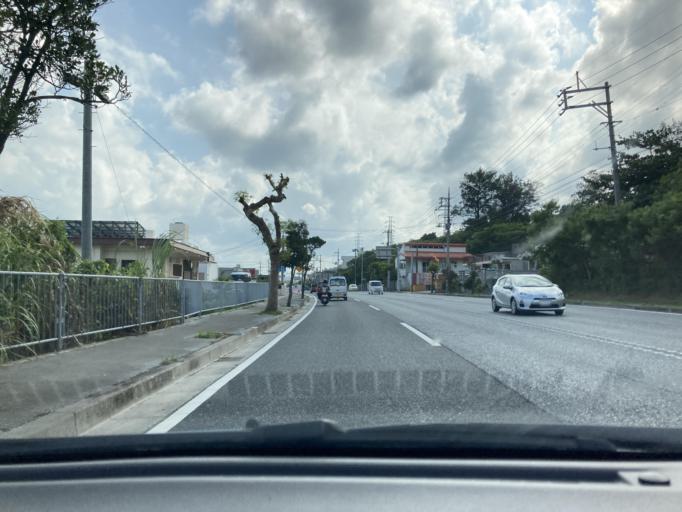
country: JP
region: Okinawa
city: Ginowan
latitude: 26.2572
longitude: 127.7855
